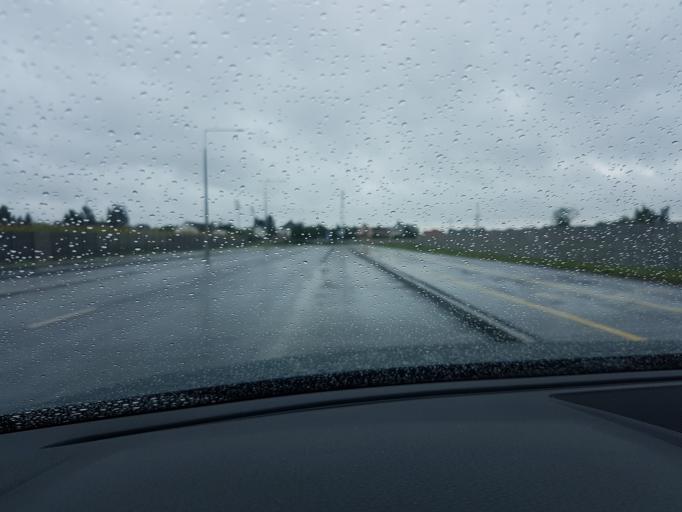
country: HU
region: Szabolcs-Szatmar-Bereg
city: Kisvarda
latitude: 48.2360
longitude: 22.0808
